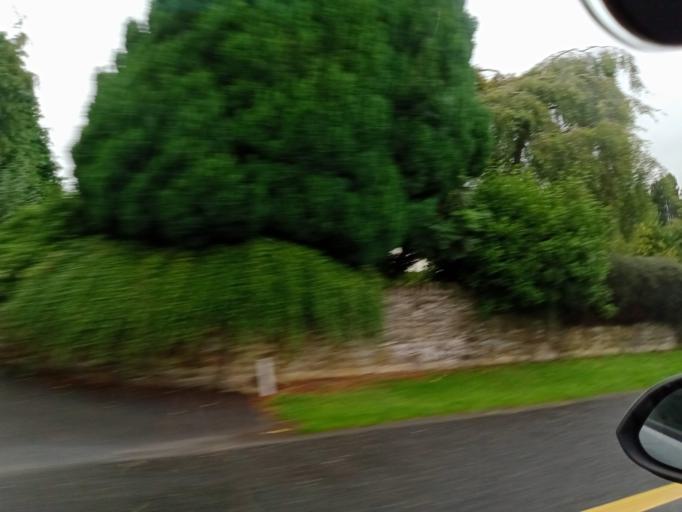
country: IE
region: Leinster
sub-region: Kilkenny
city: Castlecomer
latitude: 52.7867
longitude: -7.2114
